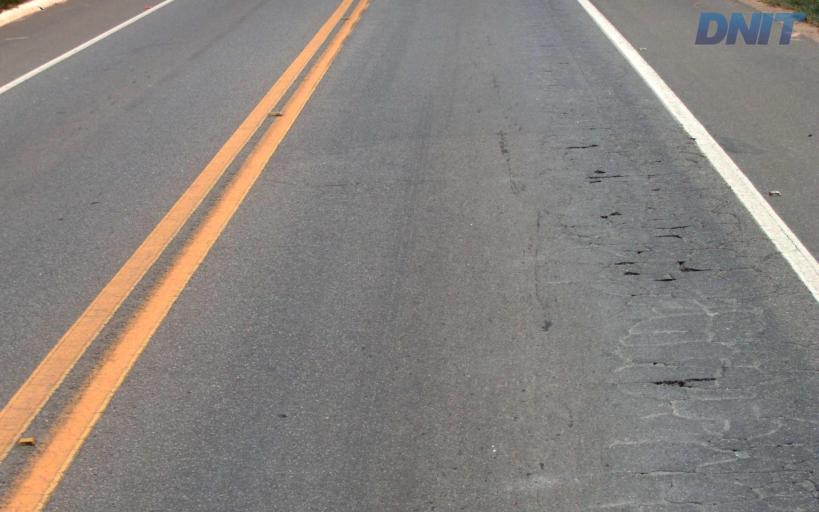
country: BR
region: Minas Gerais
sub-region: Governador Valadares
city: Governador Valadares
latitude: -18.8807
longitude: -41.9943
